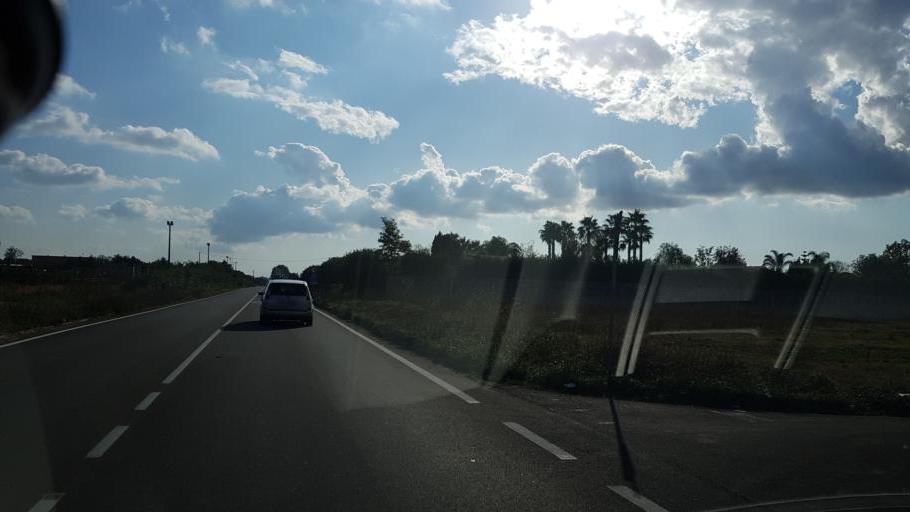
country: IT
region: Apulia
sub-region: Provincia di Lecce
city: Salice Salentino
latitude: 40.3652
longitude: 17.9674
